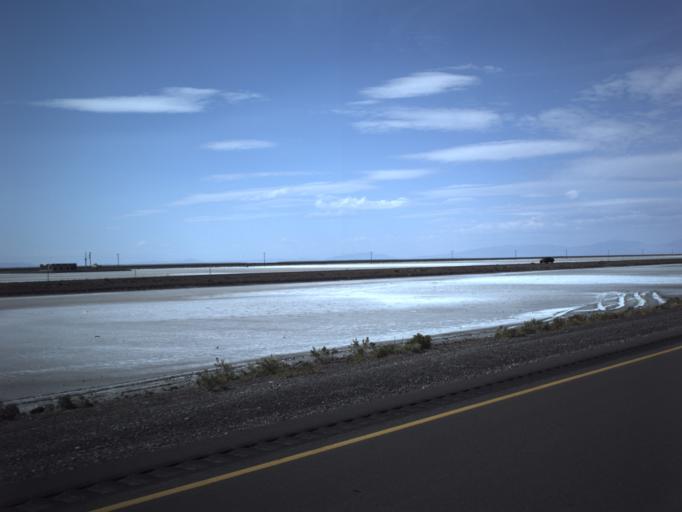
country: US
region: Utah
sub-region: Tooele County
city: Wendover
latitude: 40.7303
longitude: -113.4349
